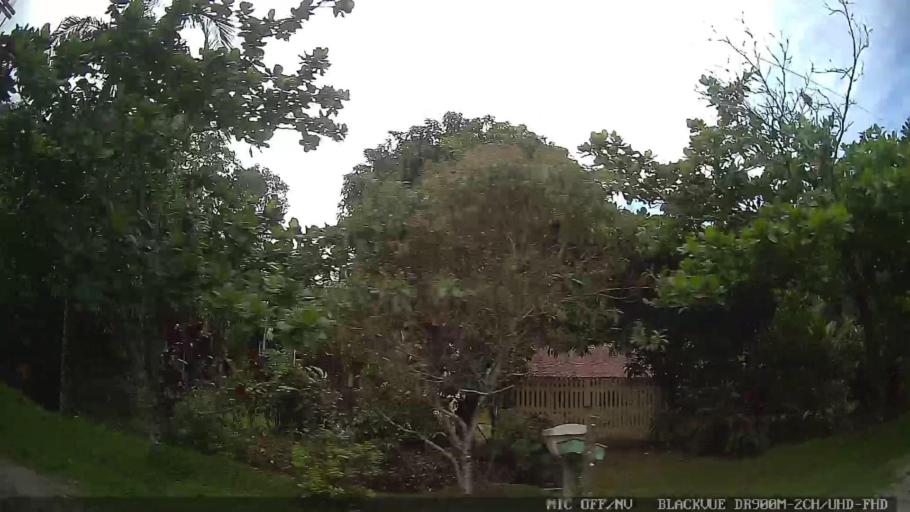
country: BR
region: Sao Paulo
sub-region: Iguape
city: Iguape
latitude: -24.6629
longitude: -47.4226
